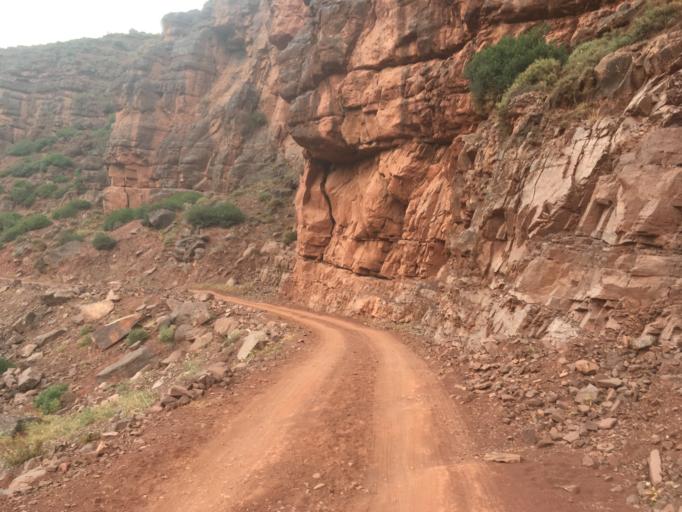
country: MA
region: Marrakech-Tensift-Al Haouz
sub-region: Al-Haouz
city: Tidili Mesfioua
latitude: 31.2688
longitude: -7.6751
